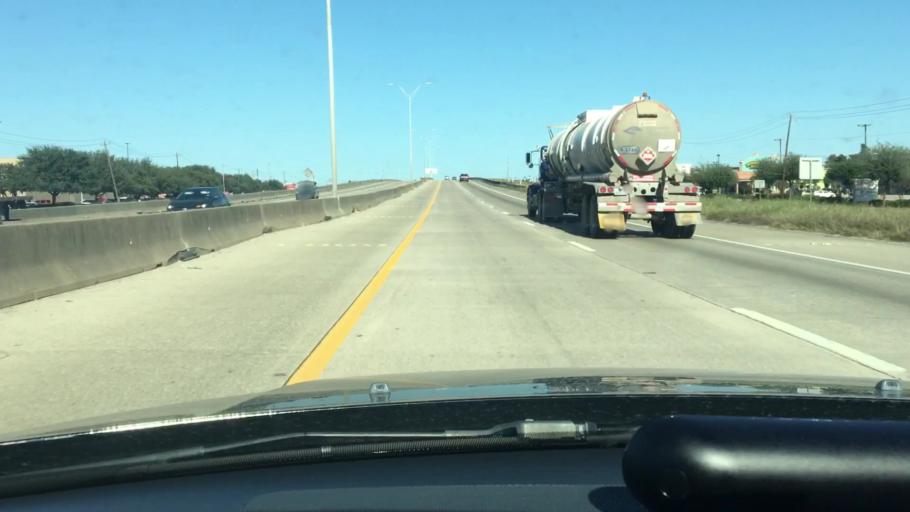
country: US
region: Texas
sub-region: Harris County
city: Cloverleaf
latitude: 29.8049
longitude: -95.1633
